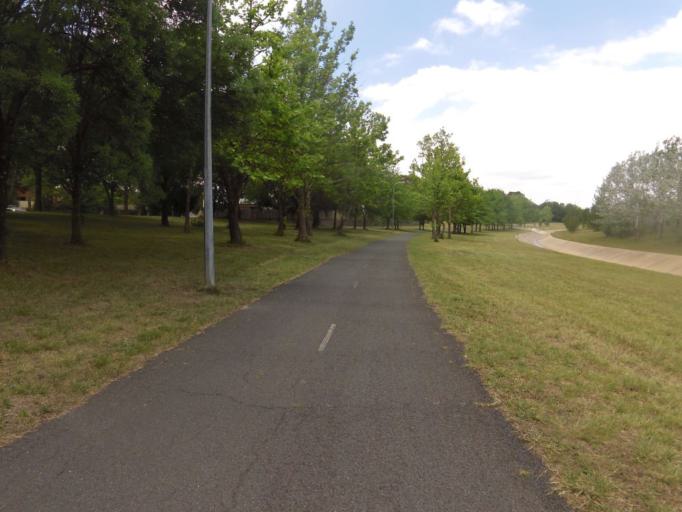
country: AU
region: Australian Capital Territory
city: Macarthur
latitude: -35.4195
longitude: 149.1059
